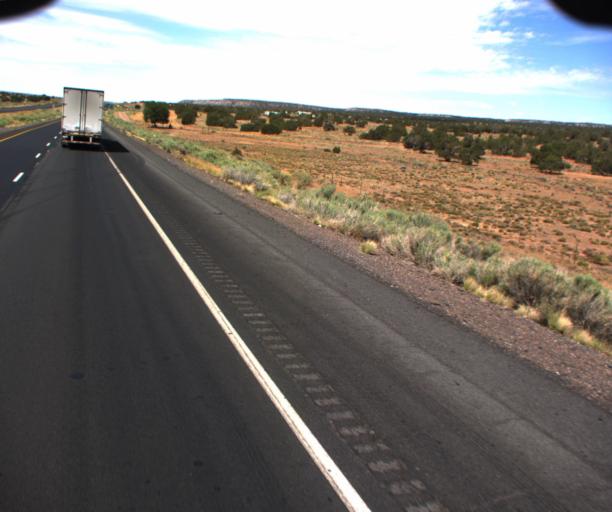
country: US
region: Arizona
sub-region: Apache County
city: Houck
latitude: 35.3142
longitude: -109.0993
